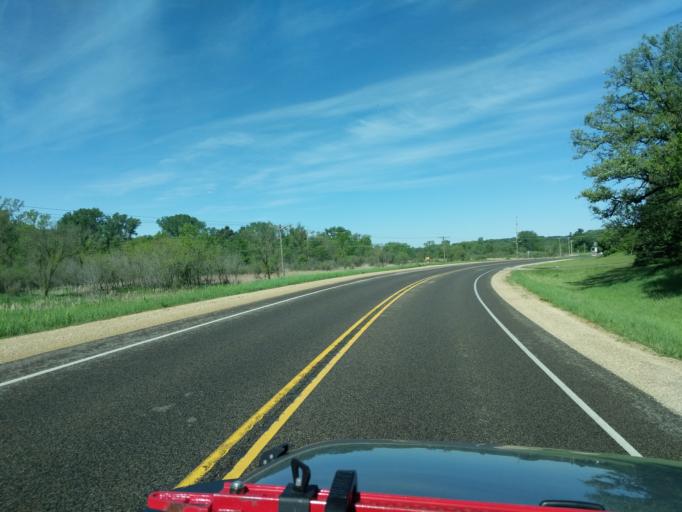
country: US
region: Wisconsin
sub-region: Pierce County
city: River Falls
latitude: 44.8495
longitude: -92.5551
